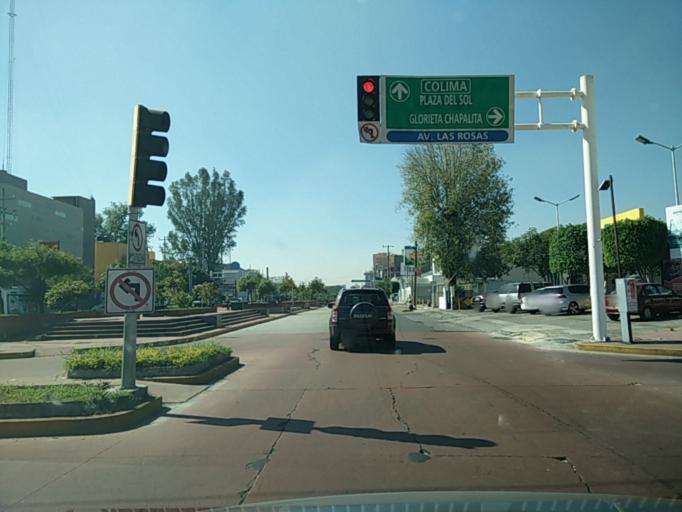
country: MX
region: Jalisco
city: Guadalajara
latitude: 20.6594
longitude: -103.3974
